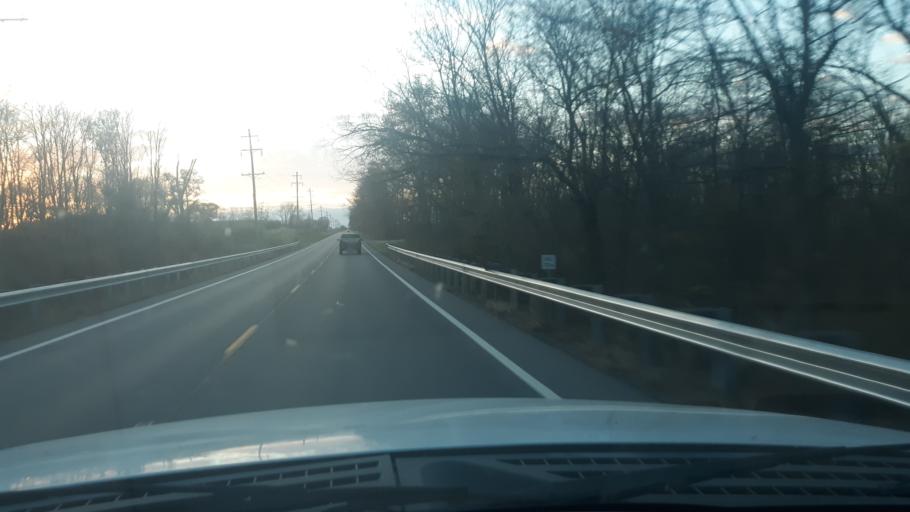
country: US
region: Illinois
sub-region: Saline County
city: Harrisburg
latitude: 37.8347
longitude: -88.5561
